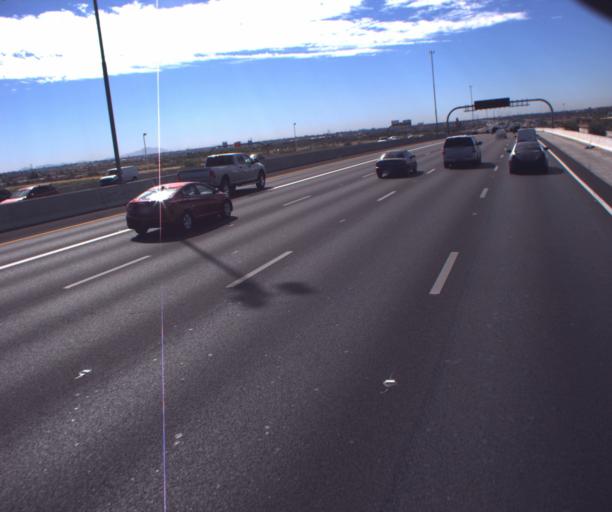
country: US
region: Arizona
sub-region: Maricopa County
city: Scottsdale
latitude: 33.4656
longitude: -111.8887
